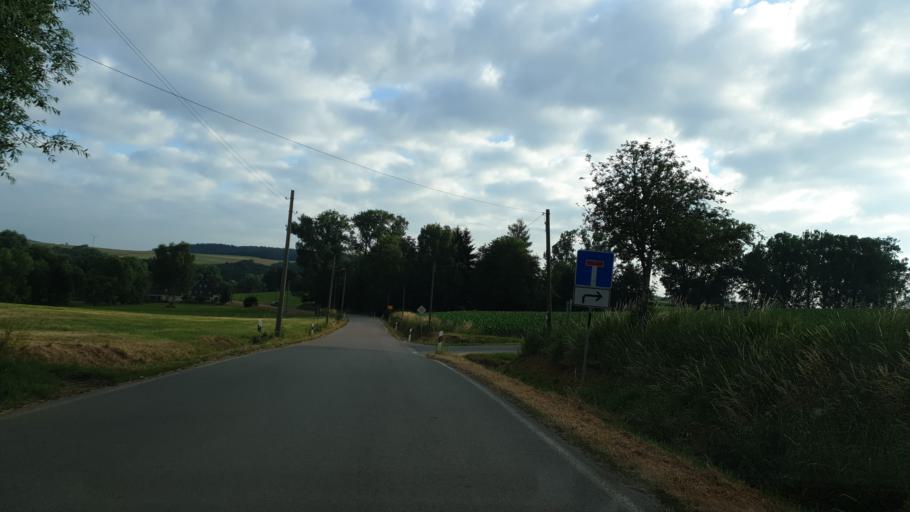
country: DE
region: Saxony
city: Sankt Egidien
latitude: 50.7770
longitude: 12.6383
